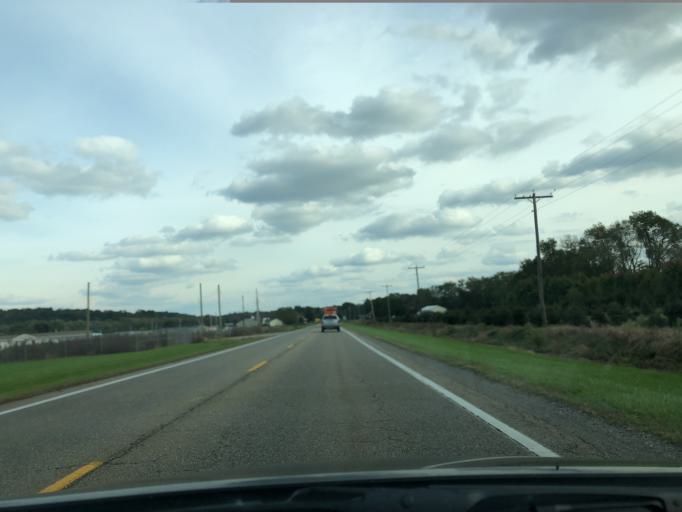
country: US
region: Ohio
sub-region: Stark County
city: Beach City
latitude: 40.6283
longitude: -81.5536
